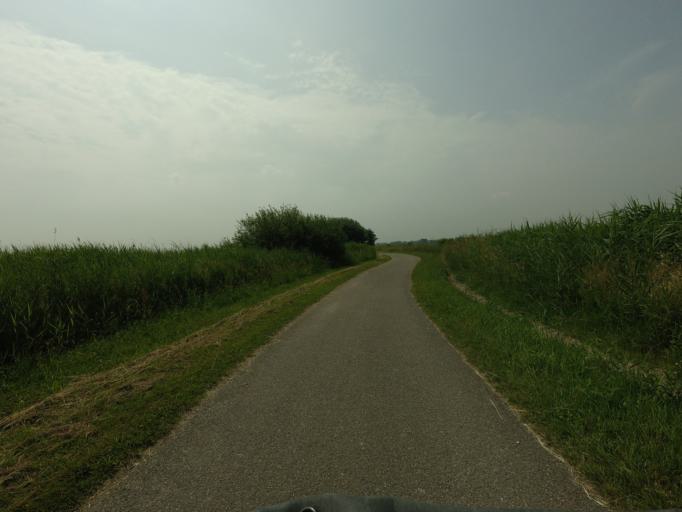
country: NL
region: South Holland
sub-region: Gemeente Krimpen aan den IJssel
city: Krimpen aan den IJssel
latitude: 51.9569
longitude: 4.6341
